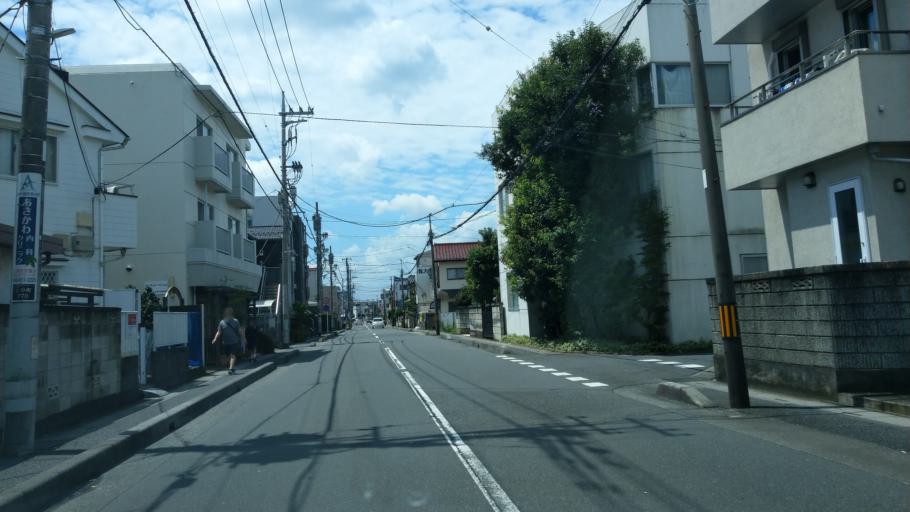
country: JP
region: Saitama
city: Yono
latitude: 35.9020
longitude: 139.6143
